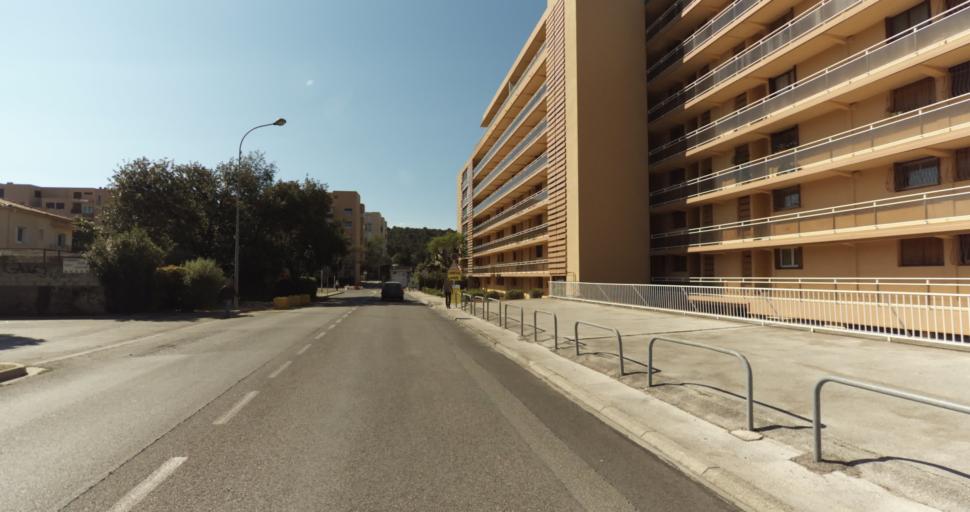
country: FR
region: Provence-Alpes-Cote d'Azur
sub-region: Departement du Var
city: La Valette-du-Var
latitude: 43.1291
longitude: 5.9877
